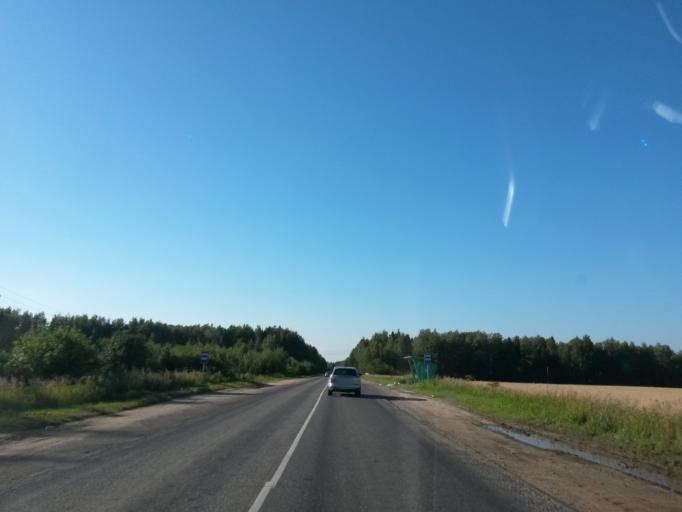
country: RU
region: Ivanovo
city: Novo-Talitsy
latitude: 57.0406
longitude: 40.7430
